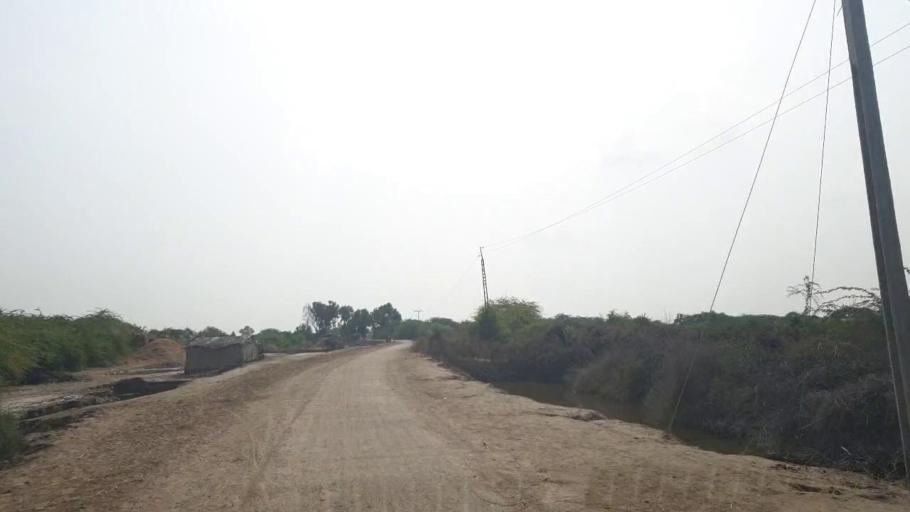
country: PK
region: Sindh
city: Badin
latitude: 24.5441
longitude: 68.6548
